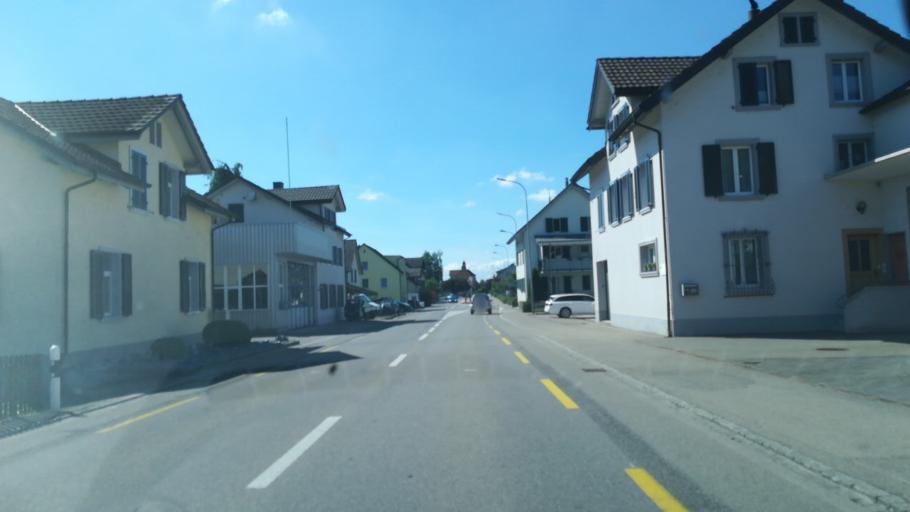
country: CH
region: Thurgau
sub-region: Weinfelden District
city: Sulgen
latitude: 47.5233
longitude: 9.2035
